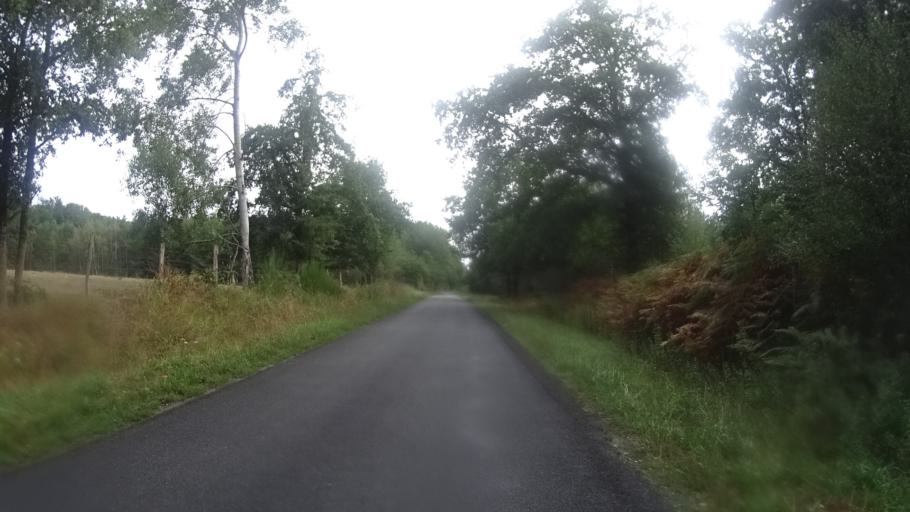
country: FR
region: Centre
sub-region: Departement du Loiret
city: Fay-aux-Loges
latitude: 47.9815
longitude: 2.1960
